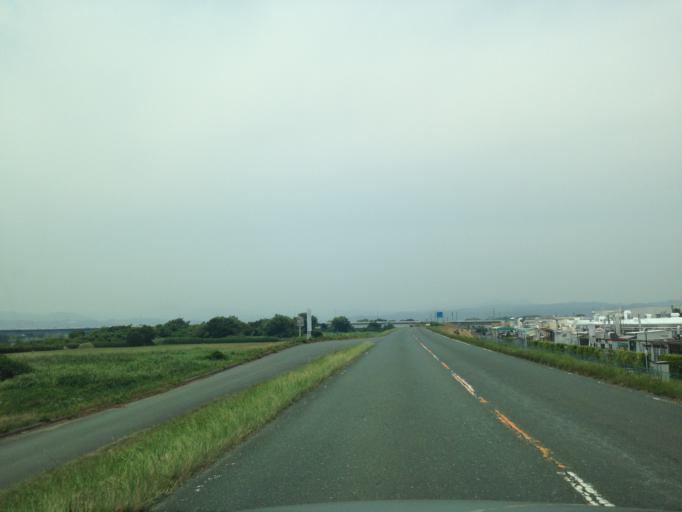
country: JP
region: Shizuoka
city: Hamakita
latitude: 34.8041
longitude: 137.8293
